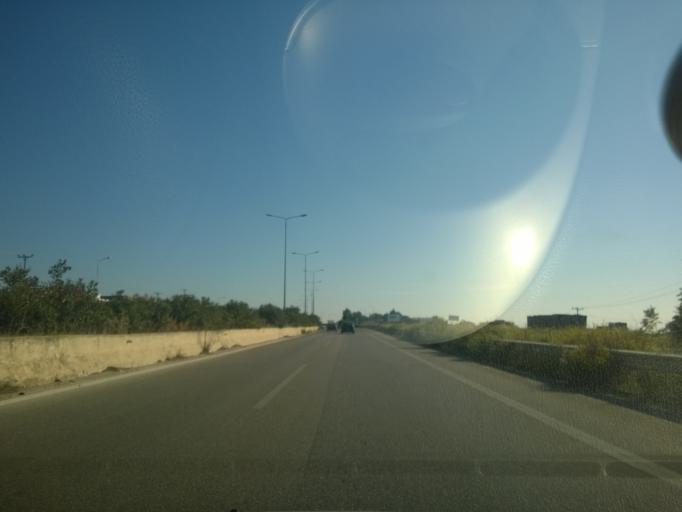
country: GR
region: Central Macedonia
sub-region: Nomos Chalkidikis
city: Lakkoma
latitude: 40.3989
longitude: 23.0316
